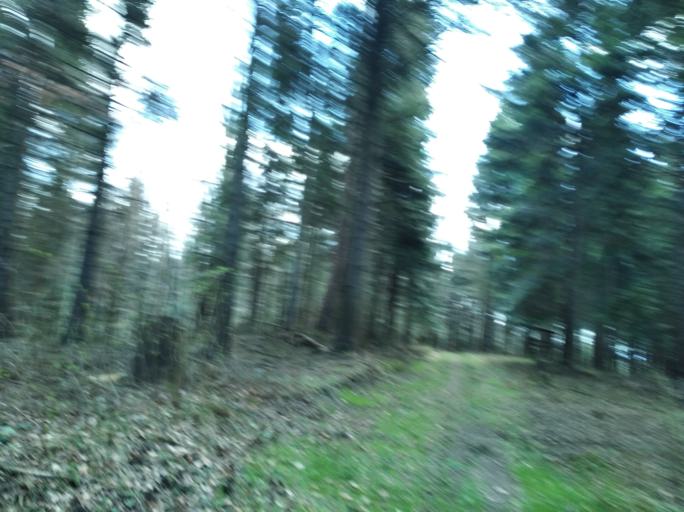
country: PL
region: Subcarpathian Voivodeship
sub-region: Powiat strzyzowski
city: Wysoka Strzyzowska
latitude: 49.8294
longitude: 21.7736
